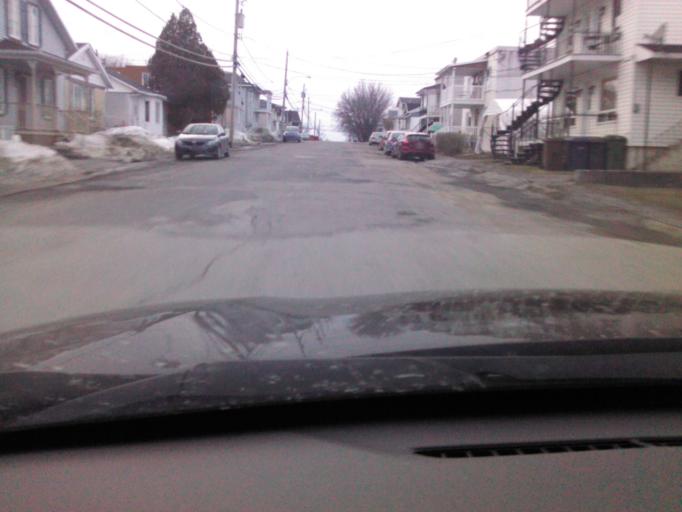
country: CA
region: Quebec
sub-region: Capitale-Nationale
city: Donnacona
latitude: 46.6742
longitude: -71.7351
